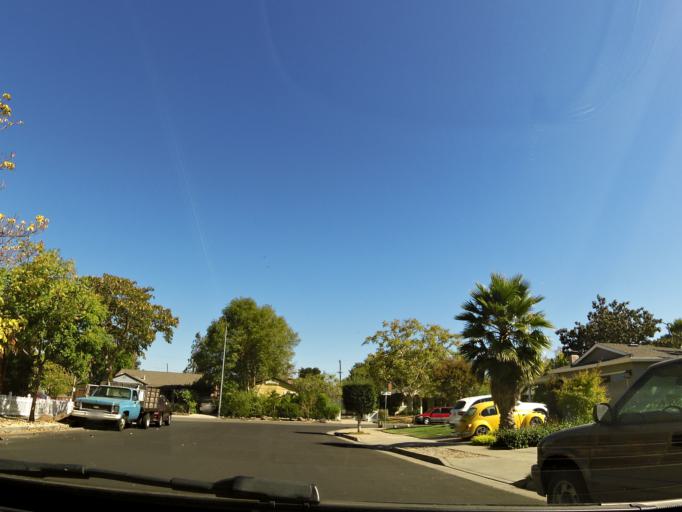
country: US
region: California
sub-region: Santa Clara County
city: Campbell
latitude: 37.2743
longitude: -121.9658
